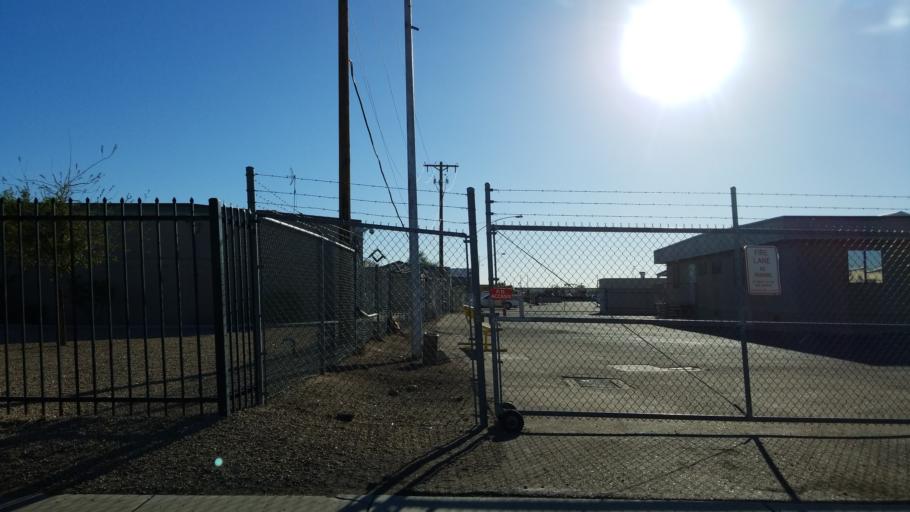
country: US
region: Arizona
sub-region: Maricopa County
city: Phoenix
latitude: 33.4264
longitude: -112.1064
